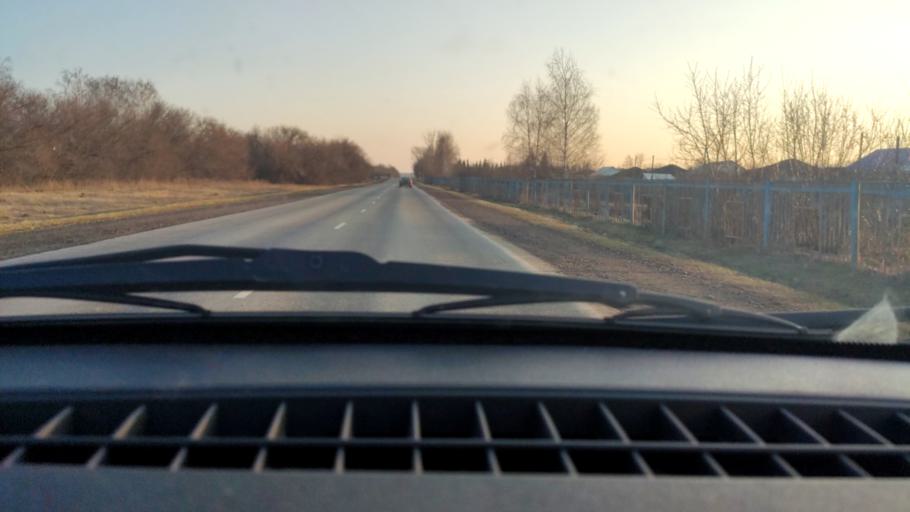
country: RU
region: Bashkortostan
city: Davlekanovo
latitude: 54.2982
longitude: 55.1293
